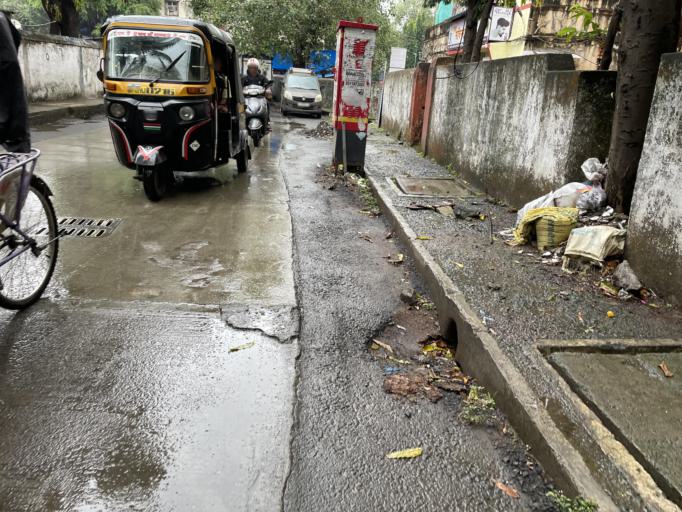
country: IN
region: Maharashtra
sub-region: Mumbai Suburban
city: Borivli
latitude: 19.2549
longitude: 72.8596
